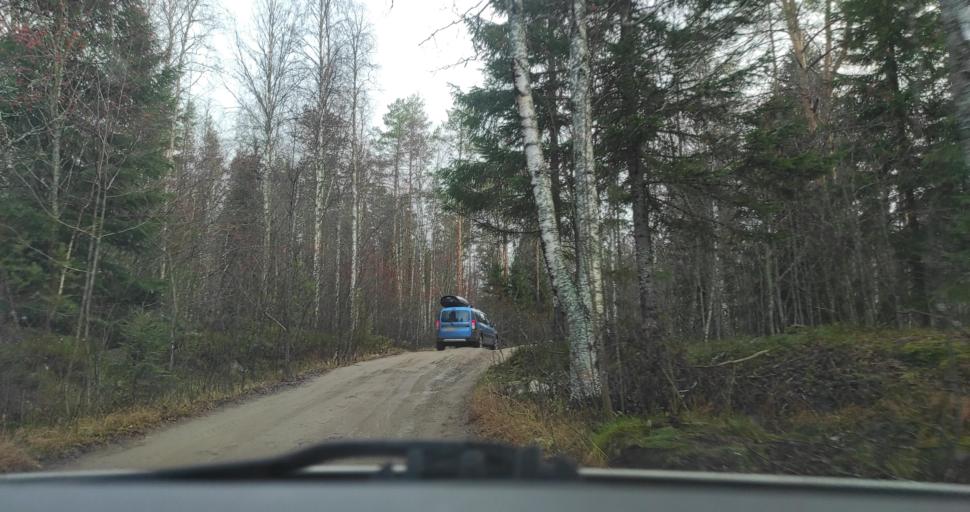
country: RU
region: Republic of Karelia
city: Pitkyaranta
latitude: 61.7370
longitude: 31.3881
